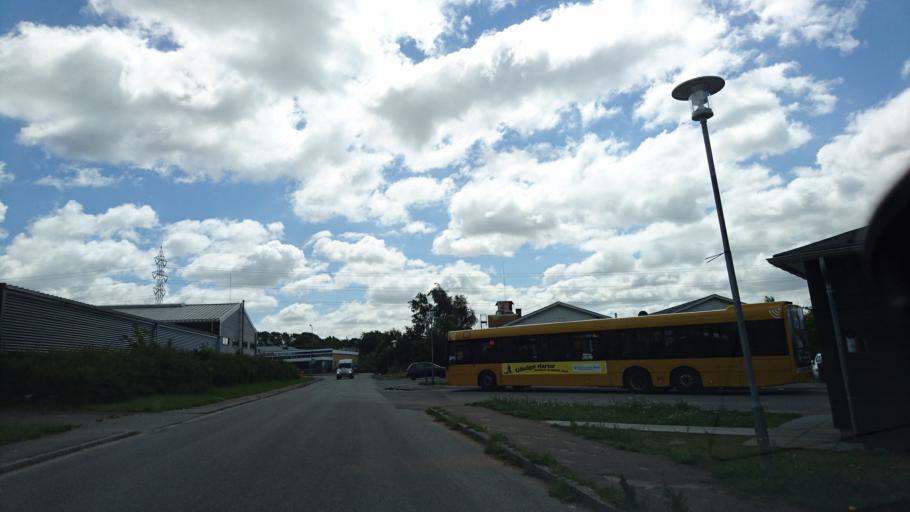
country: DK
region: Central Jutland
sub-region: Arhus Kommune
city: Stavtrup
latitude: 56.1680
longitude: 10.1174
